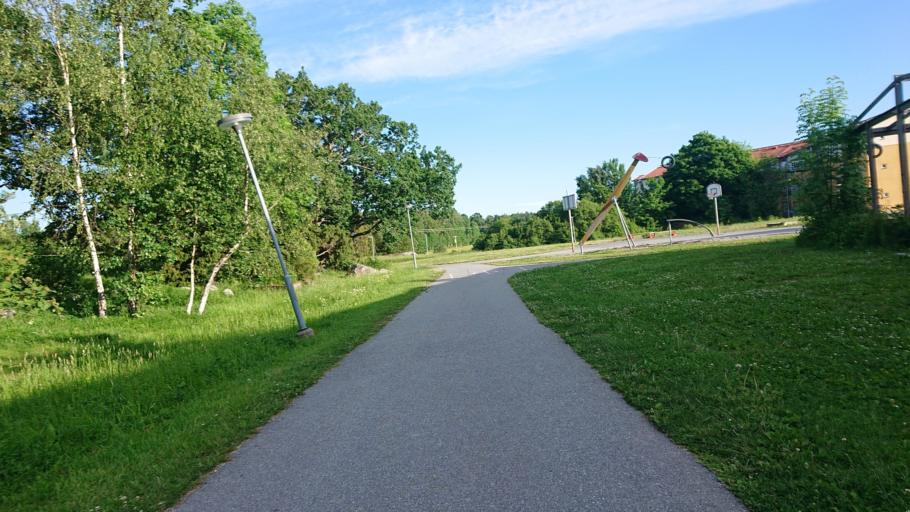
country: SE
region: Stockholm
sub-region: Osterakers Kommun
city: Akersberga
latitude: 59.5010
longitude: 18.3038
